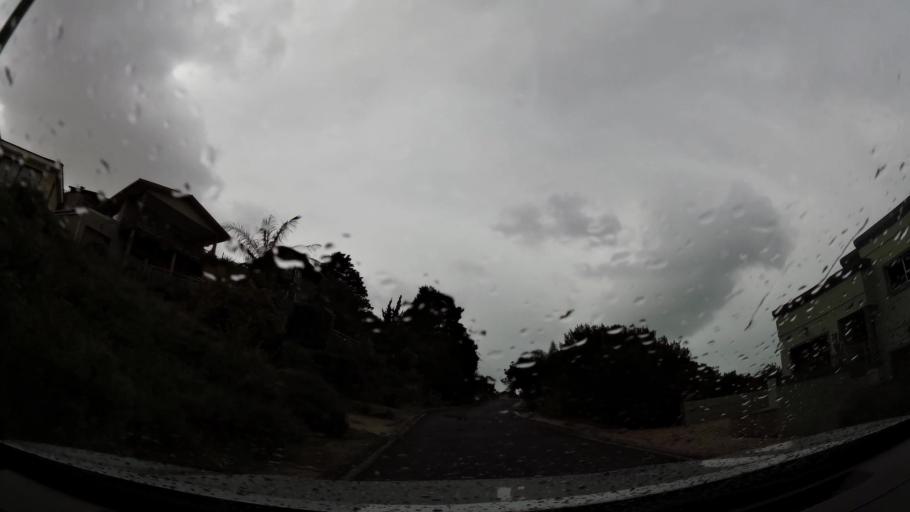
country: ZA
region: Western Cape
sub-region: Eden District Municipality
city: George
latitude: -34.0479
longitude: 22.2957
